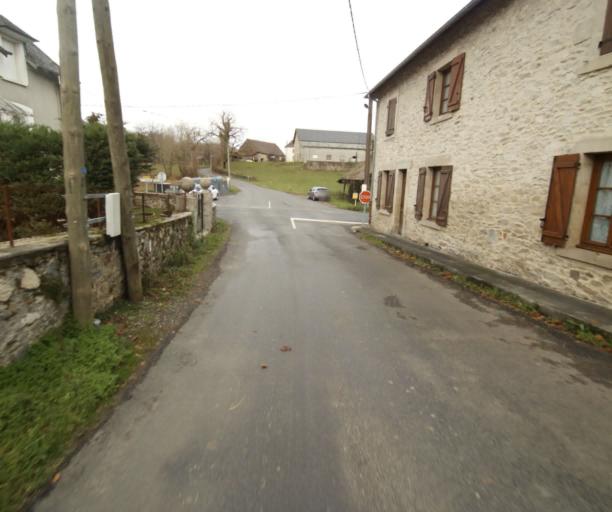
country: FR
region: Limousin
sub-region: Departement de la Correze
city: Chameyrat
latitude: 45.2466
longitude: 1.6867
